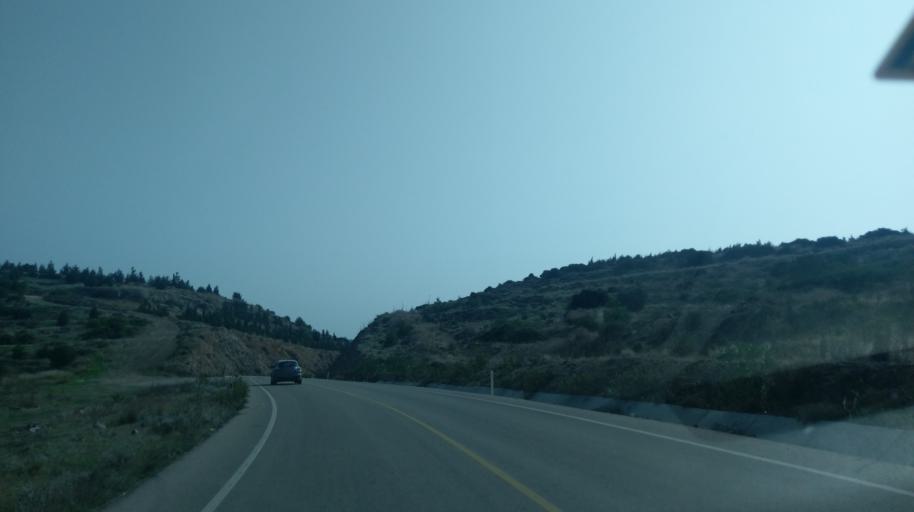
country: CY
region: Ammochostos
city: Leonarisso
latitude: 35.4818
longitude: 34.1045
